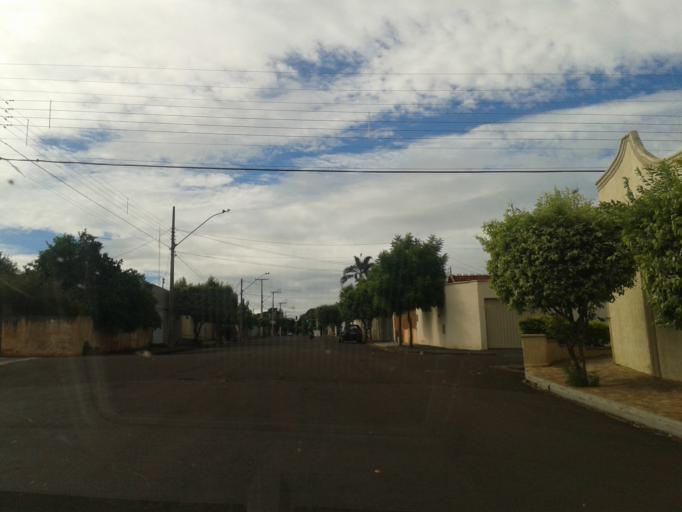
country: BR
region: Minas Gerais
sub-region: Ituiutaba
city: Ituiutaba
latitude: -18.9820
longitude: -49.4692
